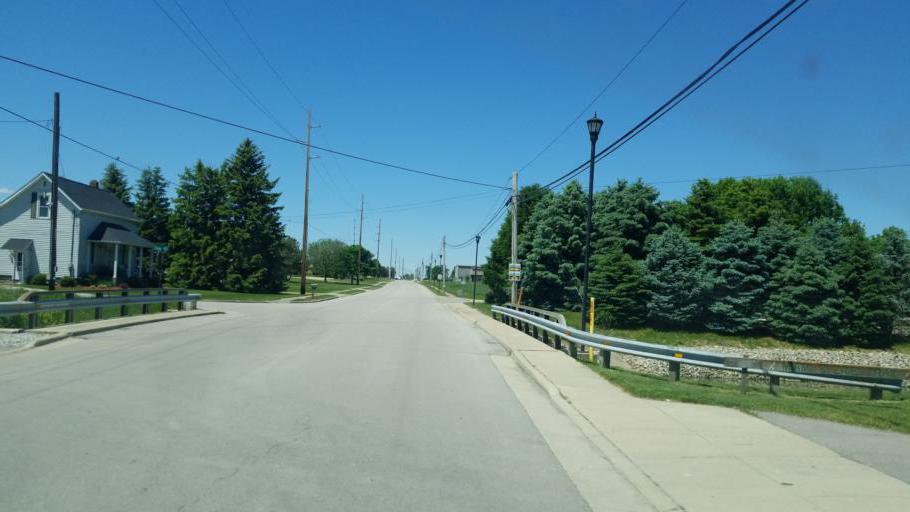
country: US
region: Ohio
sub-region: Auglaize County
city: Minster
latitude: 40.3858
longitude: -84.3832
